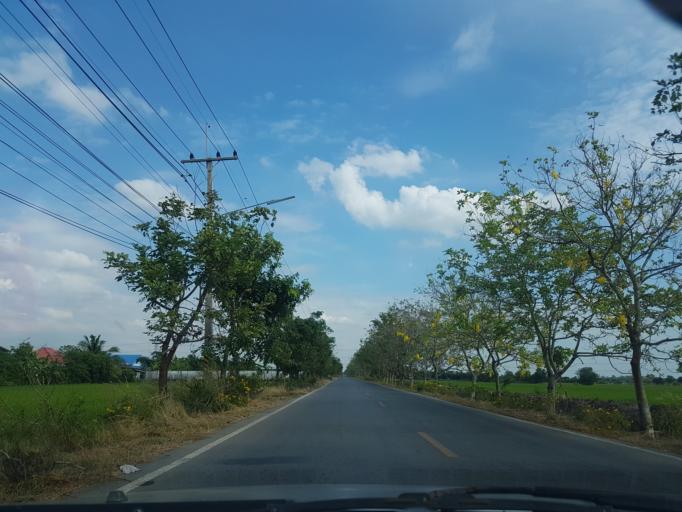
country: TH
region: Pathum Thani
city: Nong Suea
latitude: 14.1359
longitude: 100.8726
